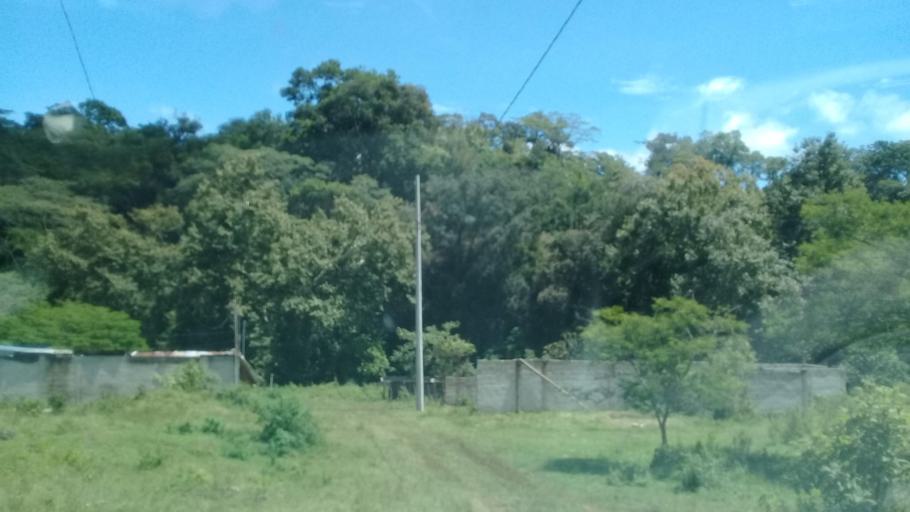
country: MX
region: Veracruz
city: El Castillo
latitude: 19.5705
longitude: -96.8808
